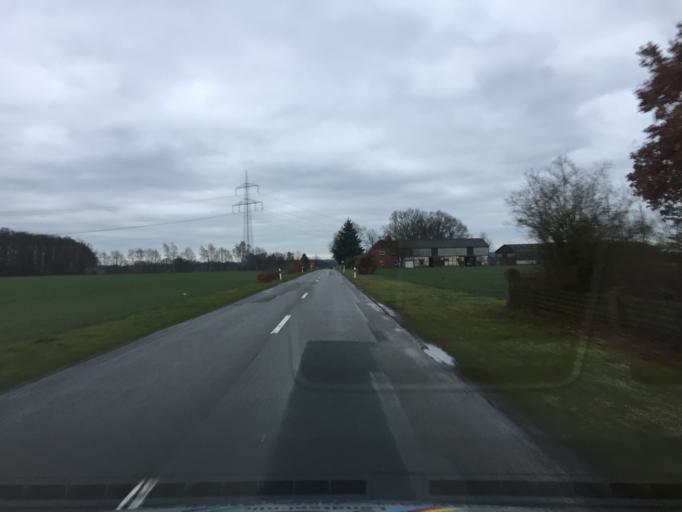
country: DE
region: Lower Saxony
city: Pennigsehl
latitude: 52.6405
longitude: 9.0038
